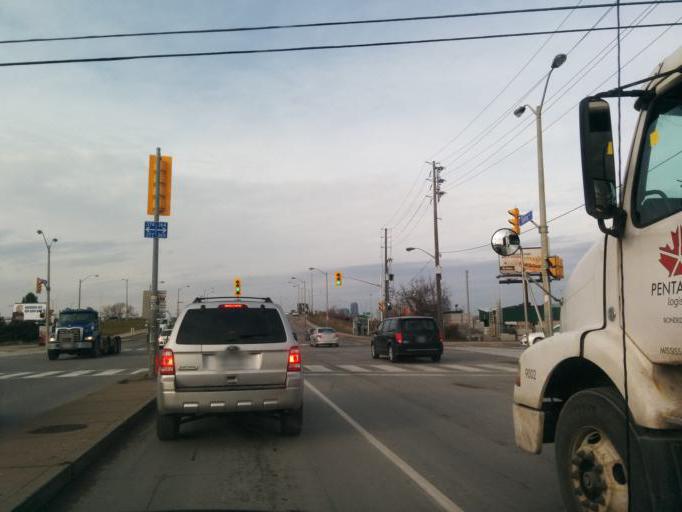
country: CA
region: Ontario
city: Etobicoke
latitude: 43.6156
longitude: -79.5244
